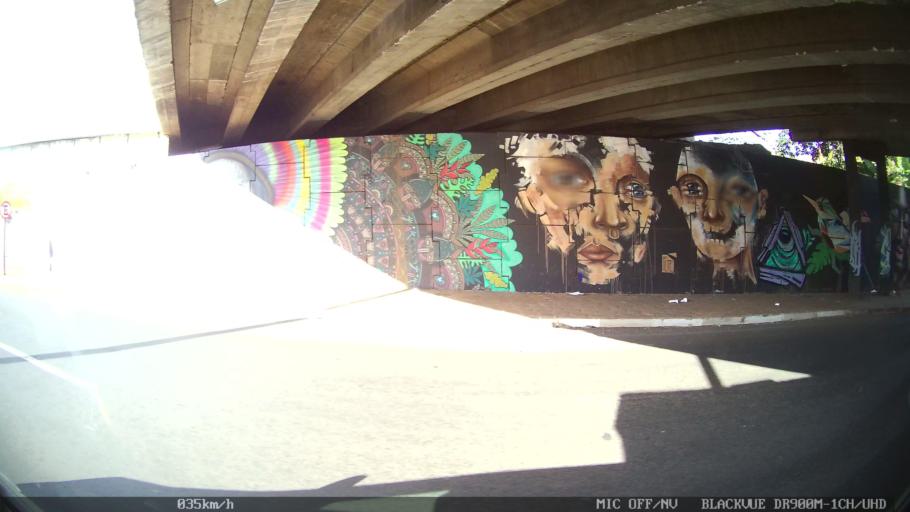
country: BR
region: Sao Paulo
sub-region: Araraquara
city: Araraquara
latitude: -21.7923
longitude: -48.1722
